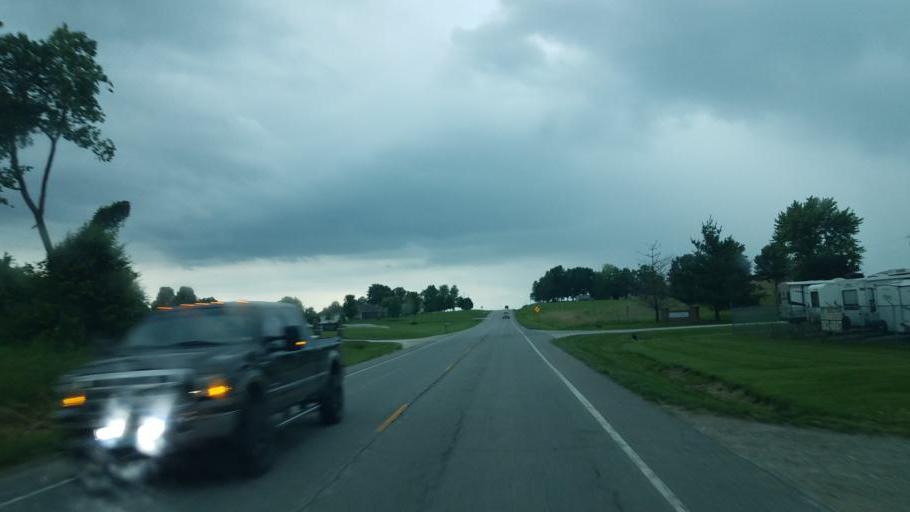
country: US
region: Missouri
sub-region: Cooper County
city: Boonville
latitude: 38.9334
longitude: -92.6904
